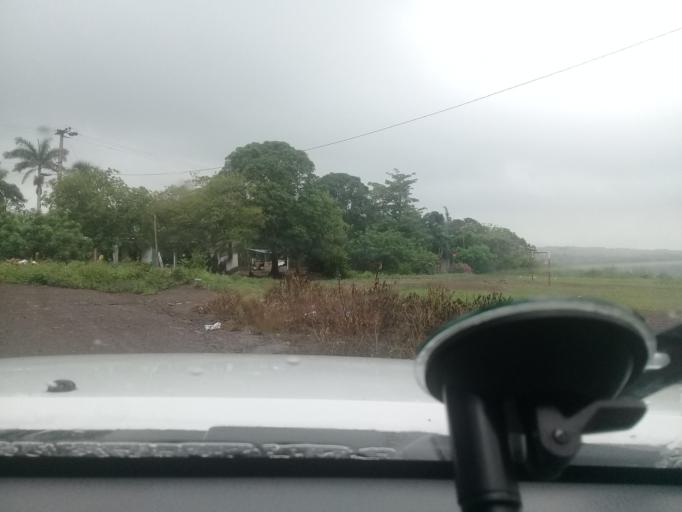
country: MX
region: Veracruz
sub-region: Puente Nacional
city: Chichicaxtle
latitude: 19.3331
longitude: -96.4246
